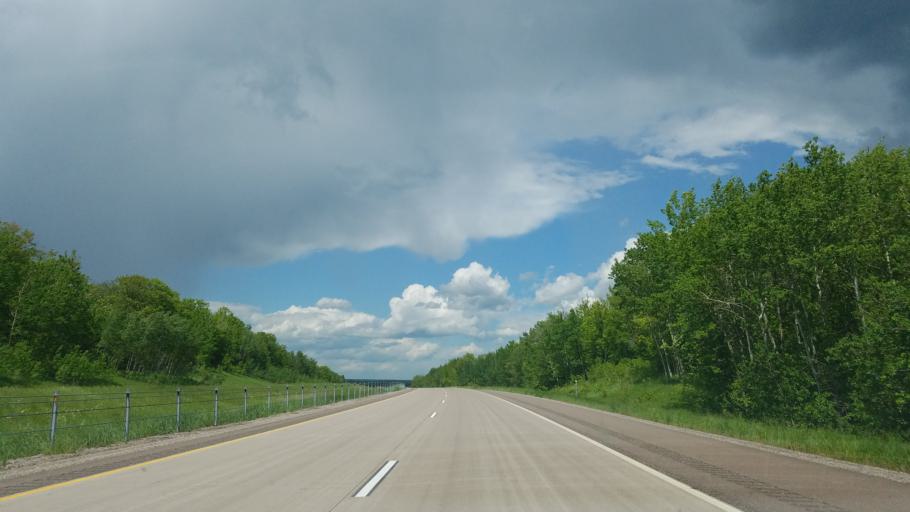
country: US
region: Minnesota
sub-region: Carlton County
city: Moose Lake
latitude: 46.4658
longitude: -92.7196
